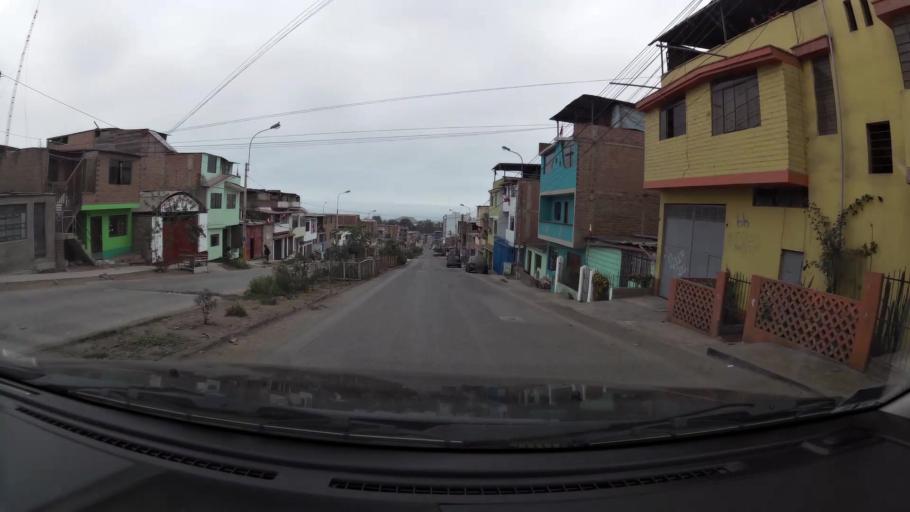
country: PE
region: Lima
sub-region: Lima
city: Surco
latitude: -12.1995
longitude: -76.9486
